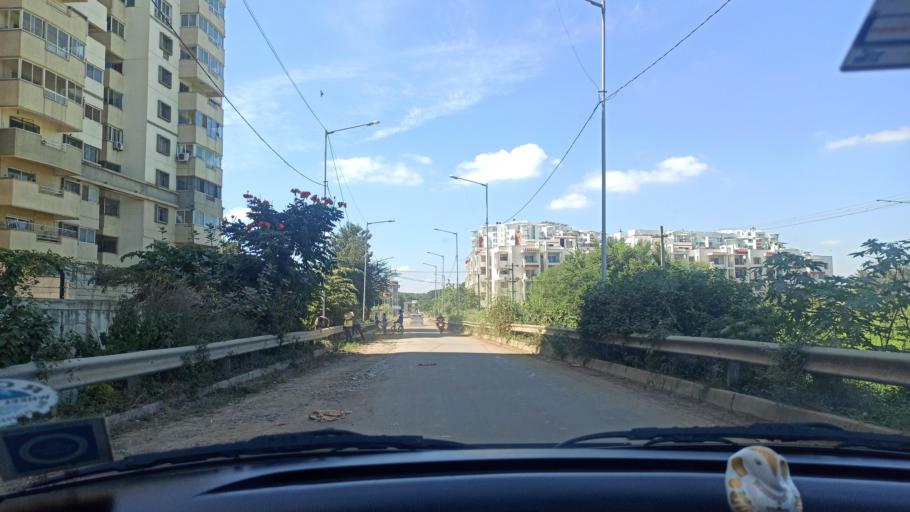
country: IN
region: Karnataka
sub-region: Bangalore Urban
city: Bangalore
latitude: 12.9270
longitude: 77.6651
